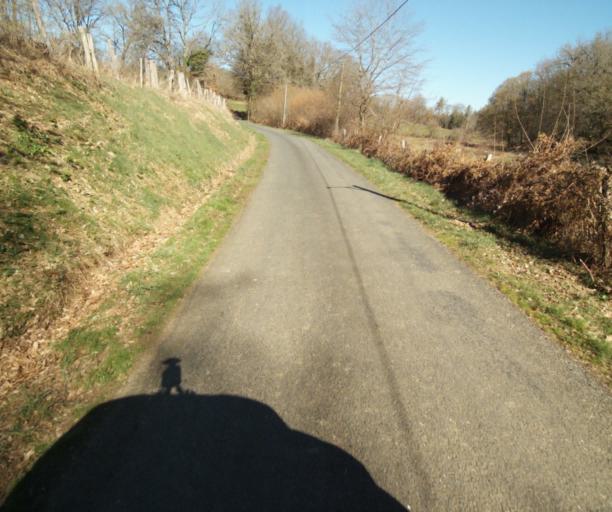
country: FR
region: Limousin
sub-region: Departement de la Correze
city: Chamboulive
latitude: 45.4133
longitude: 1.7230
